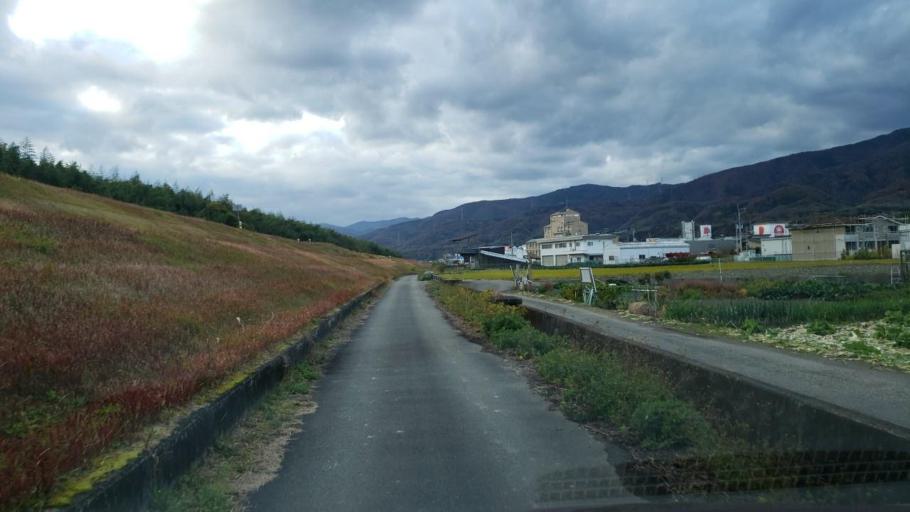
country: JP
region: Tokushima
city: Wakimachi
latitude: 34.0622
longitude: 134.1598
